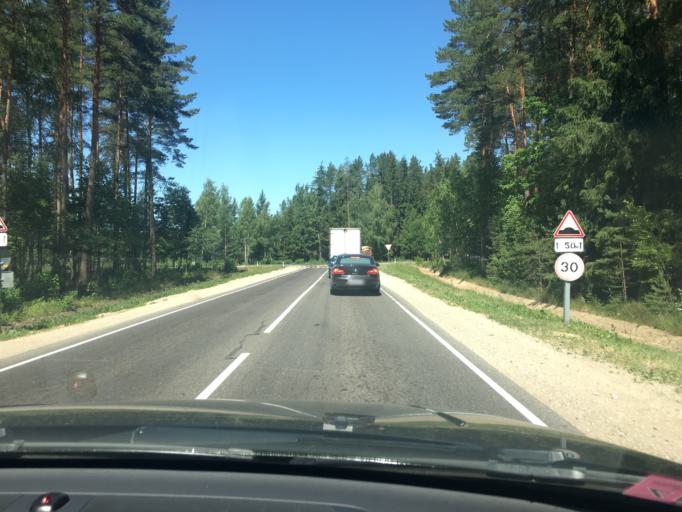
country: BY
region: Grodnenskaya
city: Iwye
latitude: 53.9411
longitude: 25.8104
